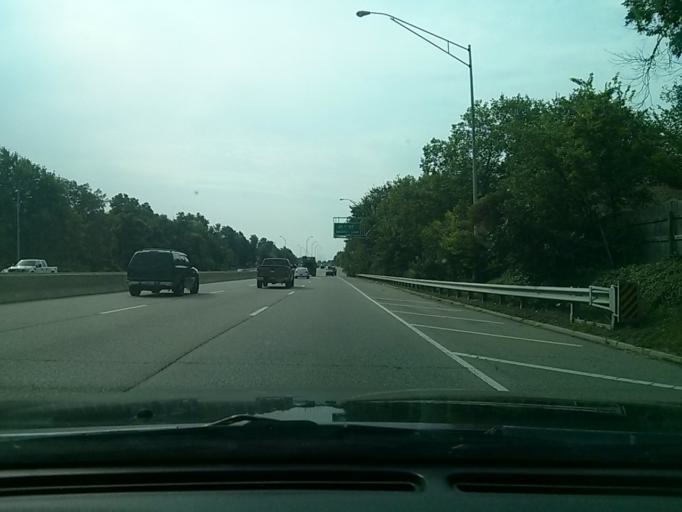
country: US
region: Oklahoma
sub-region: Tulsa County
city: Tulsa
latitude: 36.1394
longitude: -95.9538
